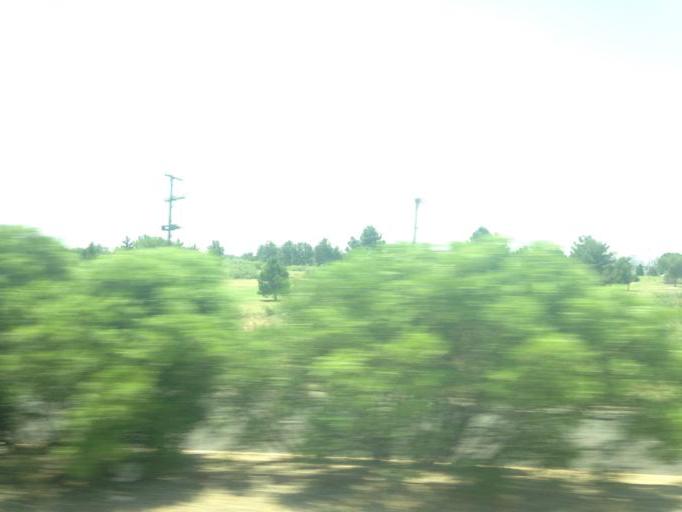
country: US
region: Texas
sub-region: Midland County
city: Midland
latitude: 32.0468
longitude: -102.0751
